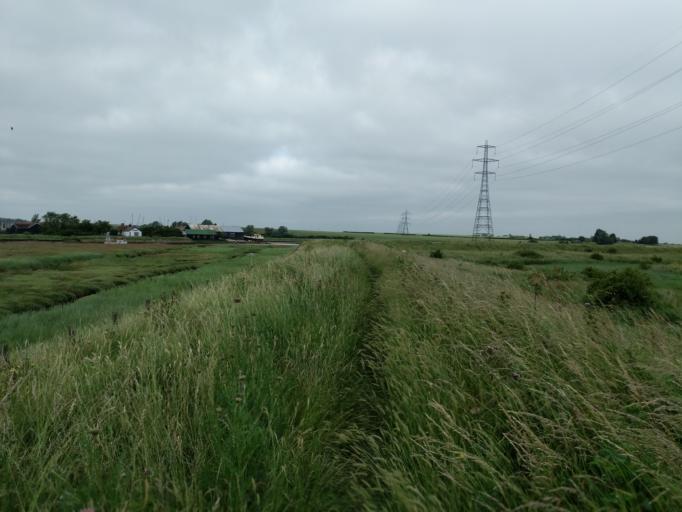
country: GB
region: England
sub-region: Kent
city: Faversham
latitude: 51.3366
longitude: 0.8988
